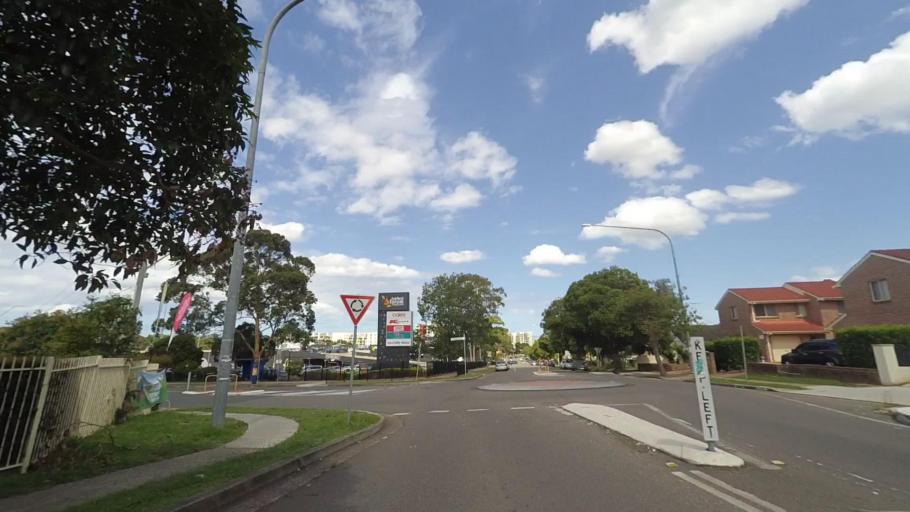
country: AU
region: New South Wales
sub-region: Fairfield
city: Fairfield Heights
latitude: -33.8673
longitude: 150.9505
